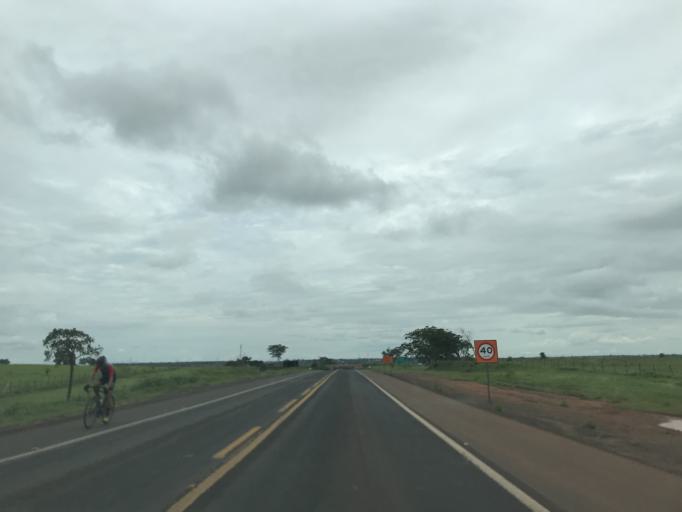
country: BR
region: Sao Paulo
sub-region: Nova Granada
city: Nova Granada
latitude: -20.3292
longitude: -49.2126
